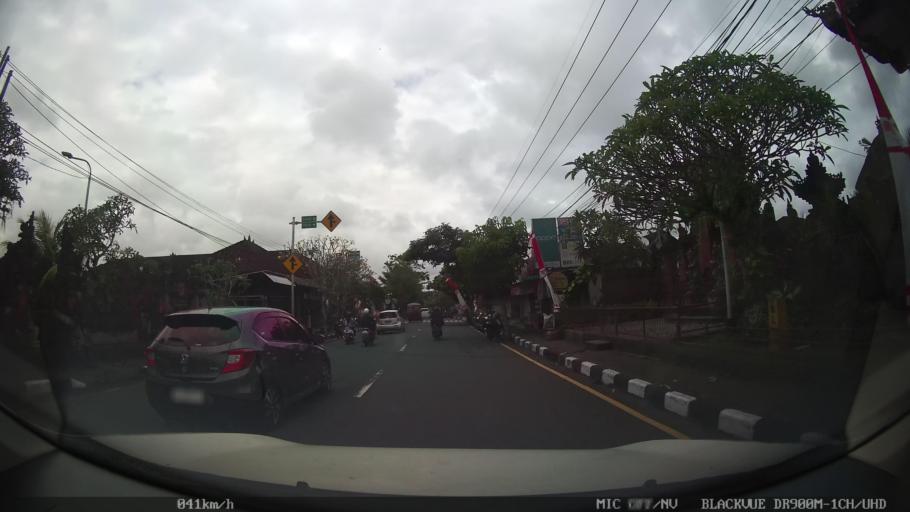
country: ID
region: Bali
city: Banjar Serangan
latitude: -8.5459
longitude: 115.1701
